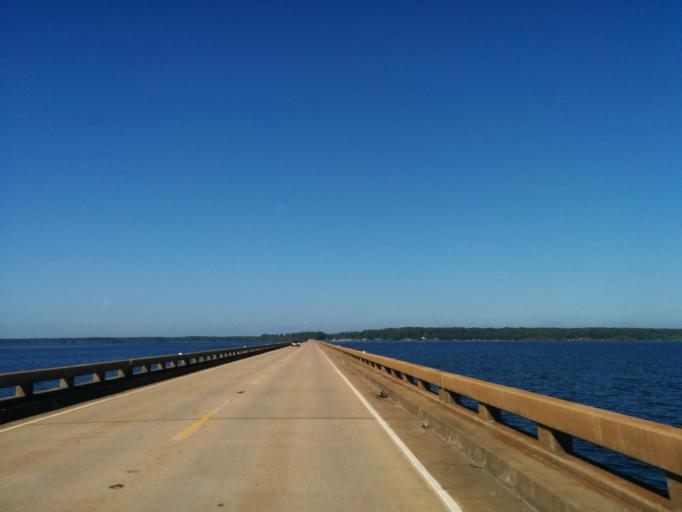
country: US
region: Texas
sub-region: Sabine County
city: Milam
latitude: 31.4752
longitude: -93.7310
